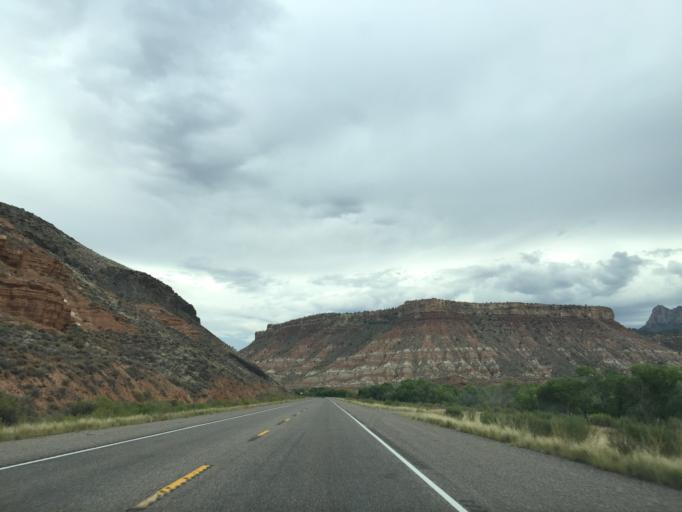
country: US
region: Utah
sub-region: Washington County
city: LaVerkin
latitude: 37.1715
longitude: -113.1085
